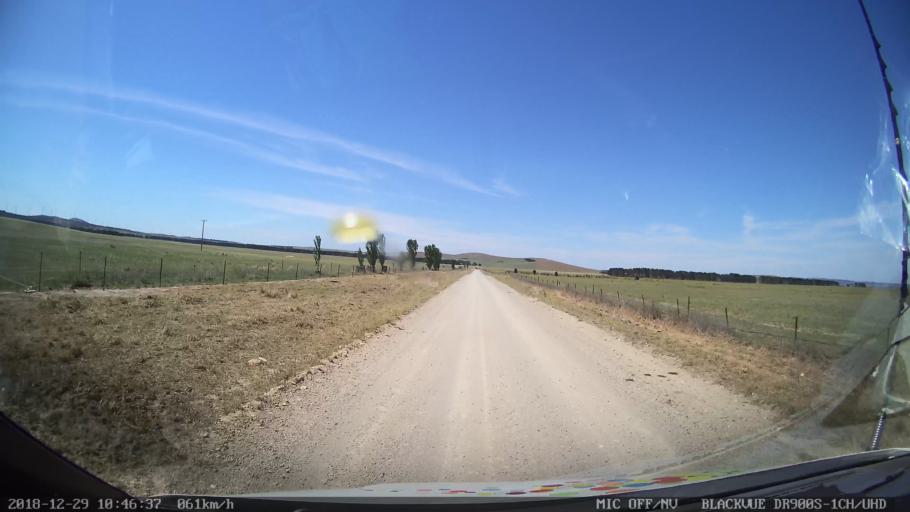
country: AU
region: New South Wales
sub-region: Palerang
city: Bungendore
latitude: -35.0519
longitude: 149.5164
